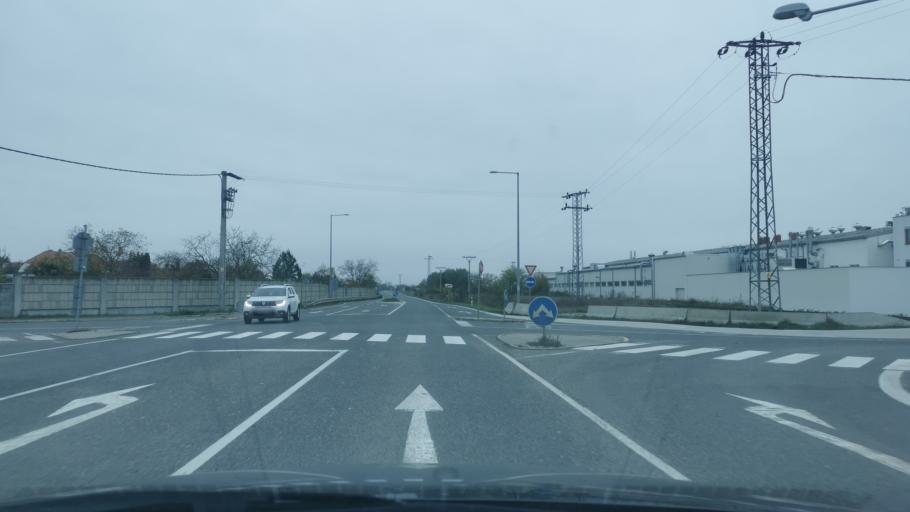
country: SK
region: Trnavsky
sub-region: Okres Skalica
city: Skalica
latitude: 48.8476
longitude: 17.2162
